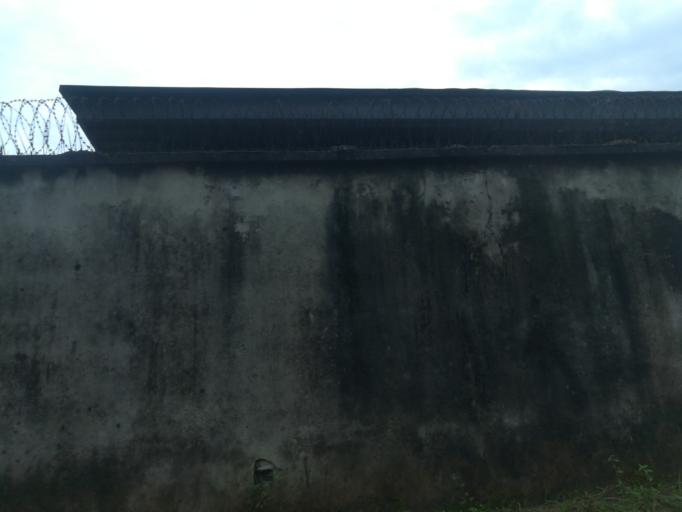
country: NG
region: Rivers
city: Port Harcourt
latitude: 4.7936
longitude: 6.9610
